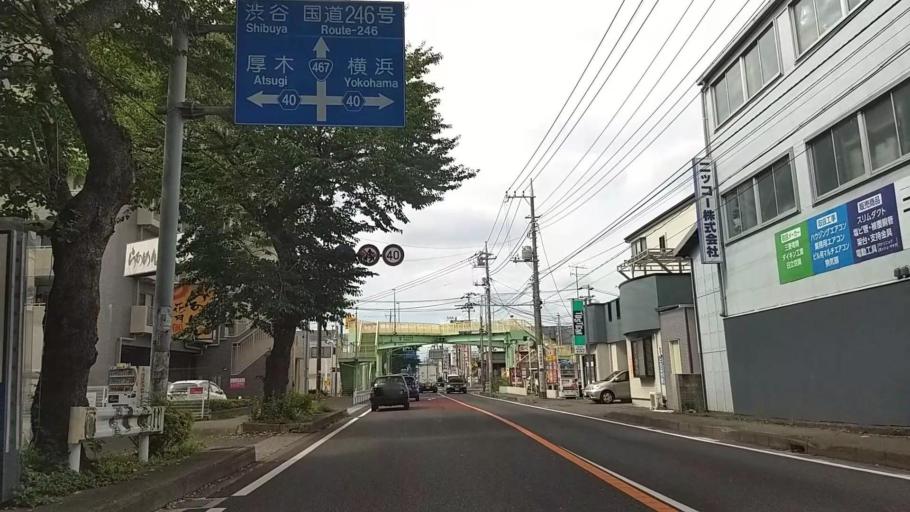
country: JP
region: Kanagawa
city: Minami-rinkan
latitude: 35.4625
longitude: 139.4673
